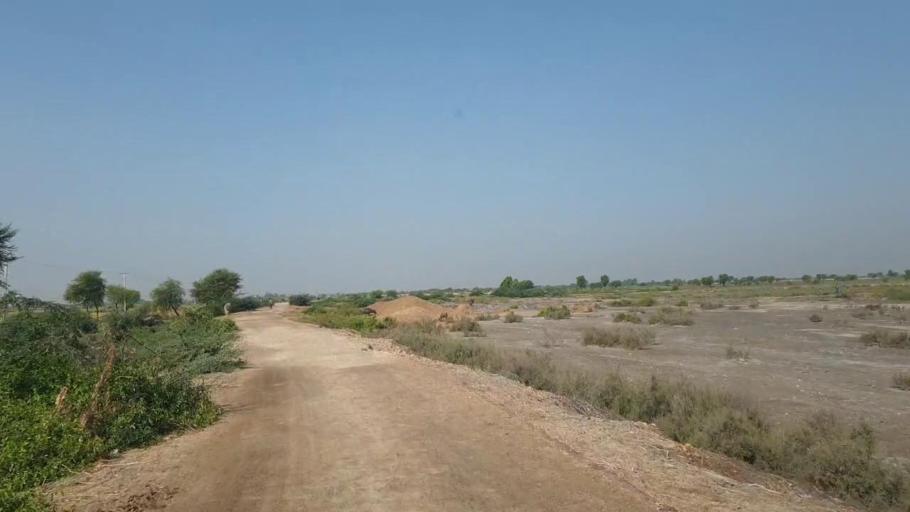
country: PK
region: Sindh
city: Badin
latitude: 24.5195
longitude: 68.7765
